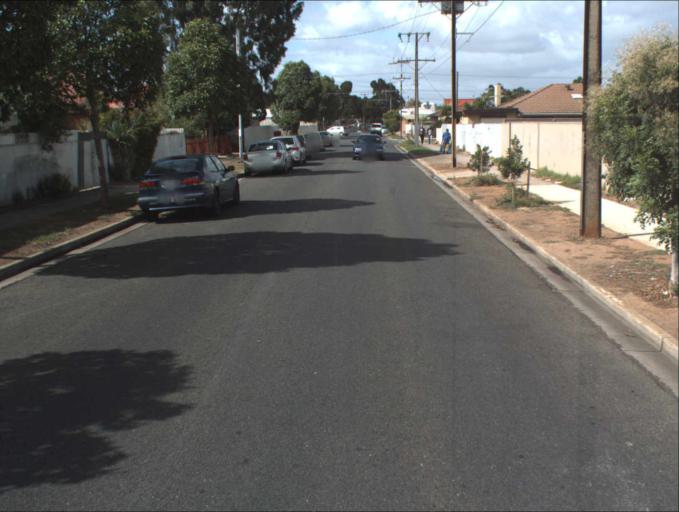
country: AU
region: South Australia
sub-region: Charles Sturt
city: Woodville North
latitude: -34.8705
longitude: 138.5518
